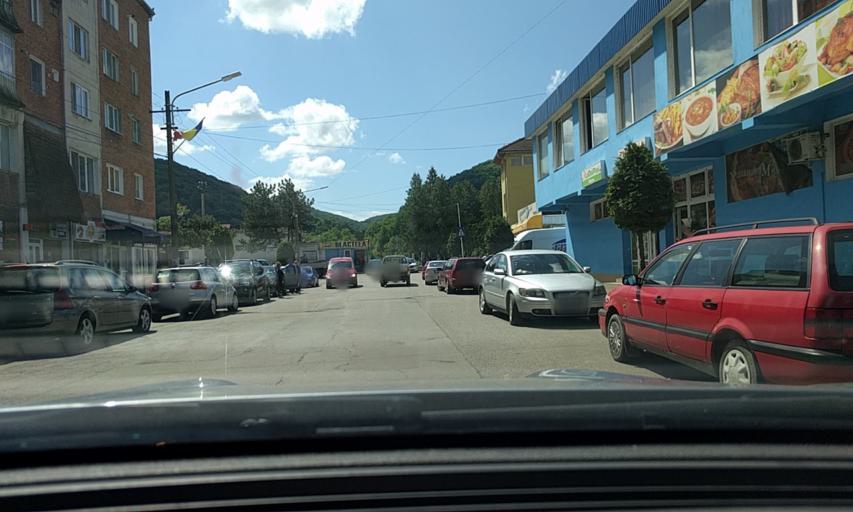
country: RO
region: Bistrita-Nasaud
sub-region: Oras Nasaud
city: Nasaud
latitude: 47.2821
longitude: 24.4115
